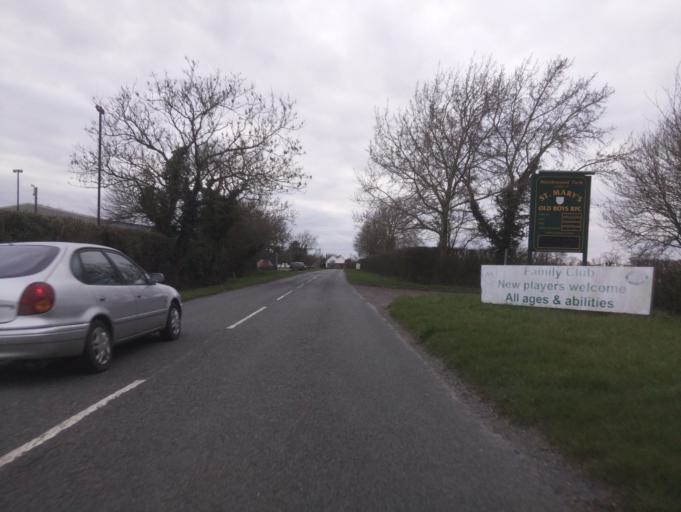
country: GB
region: England
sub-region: South Gloucestershire
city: Stoke Gifford
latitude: 51.5376
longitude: -2.5283
